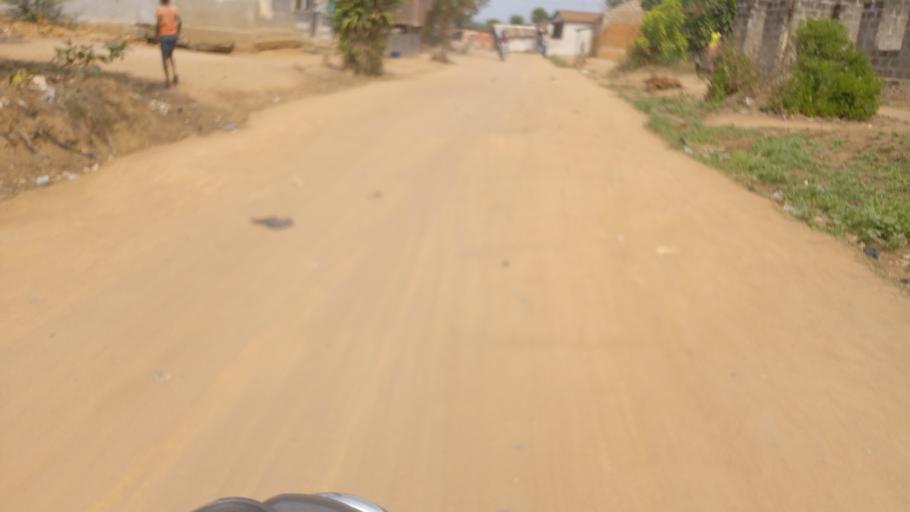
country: SL
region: Western Area
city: Waterloo
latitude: 8.3226
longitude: -13.0564
